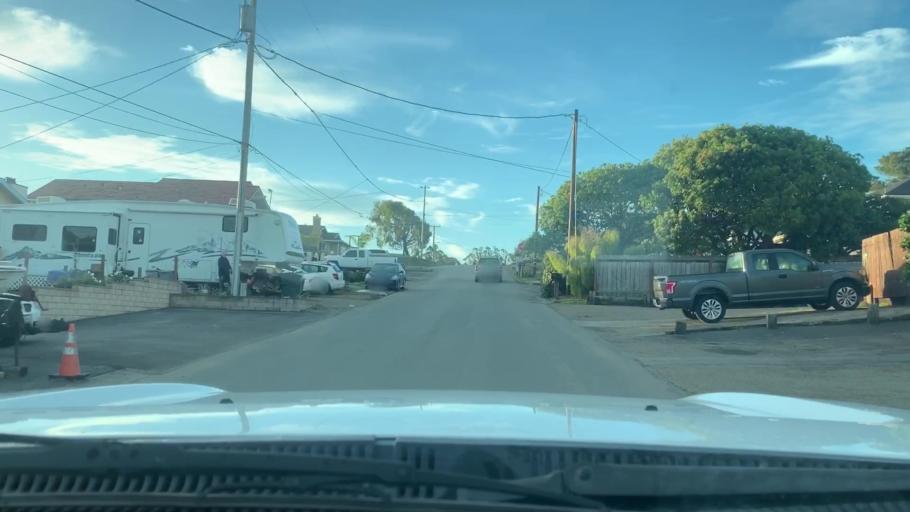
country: US
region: California
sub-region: San Luis Obispo County
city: Los Osos
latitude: 35.3233
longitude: -120.8255
